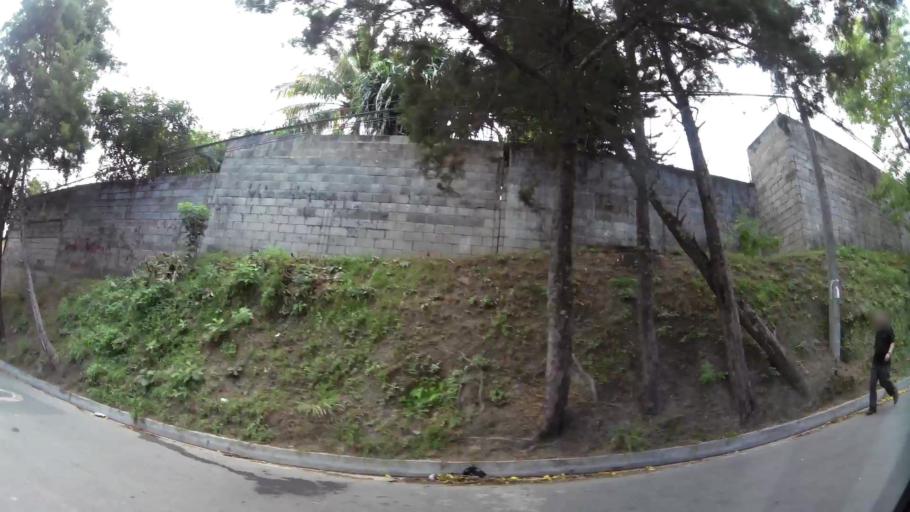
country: SV
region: San Salvador
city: Mejicanos
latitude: 13.7152
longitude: -89.2475
